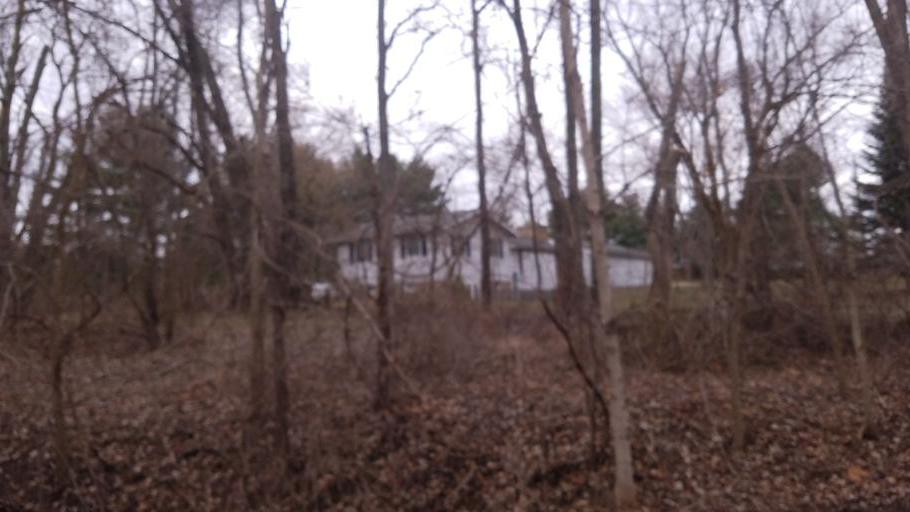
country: US
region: Ohio
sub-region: Knox County
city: Centerburg
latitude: 40.4226
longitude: -82.6529
